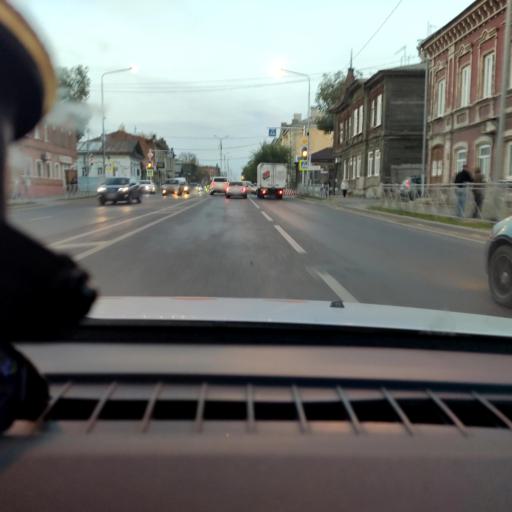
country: RU
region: Samara
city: Rozhdestveno
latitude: 53.1799
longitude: 50.0865
